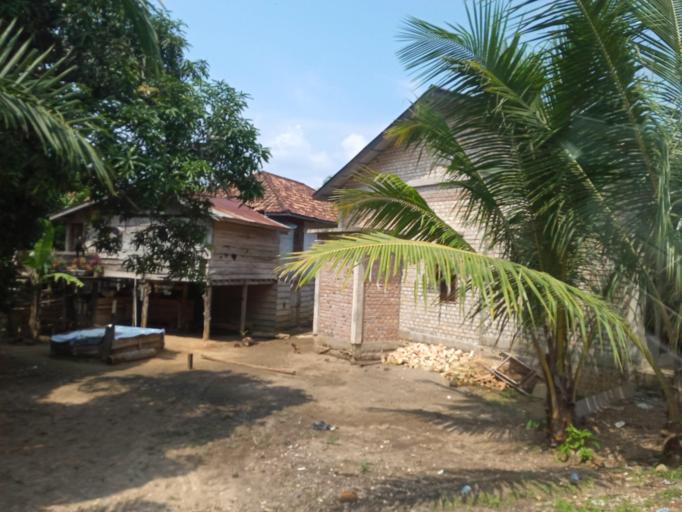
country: ID
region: Jambi
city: Mersam
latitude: -1.7064
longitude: 102.8853
